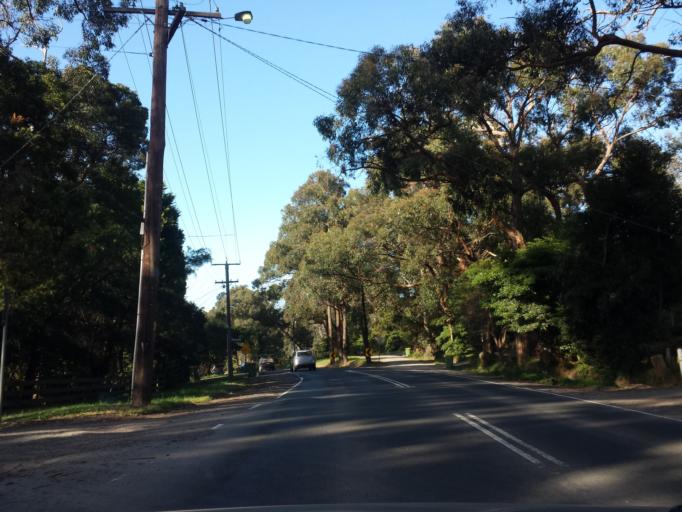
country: AU
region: Victoria
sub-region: Yarra Ranges
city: Belgrave Heights
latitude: -37.9346
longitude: 145.3564
